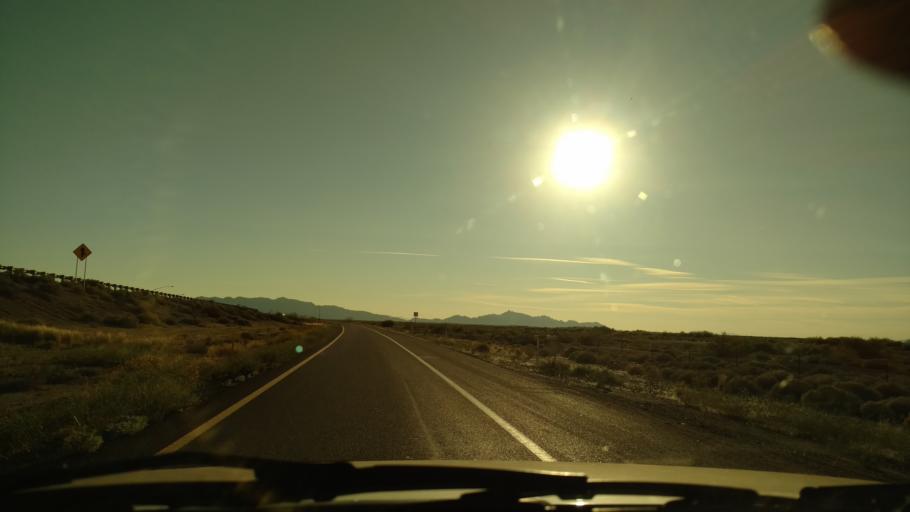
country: US
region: Arizona
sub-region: Yuma County
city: Wellton
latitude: 32.8007
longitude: -113.5420
